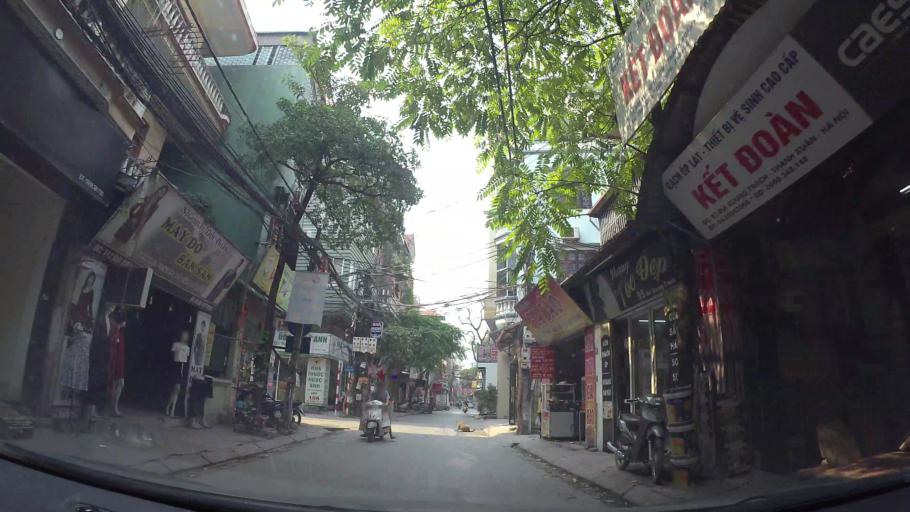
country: VN
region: Ha Noi
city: Thanh Xuan
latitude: 20.9896
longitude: 105.8178
